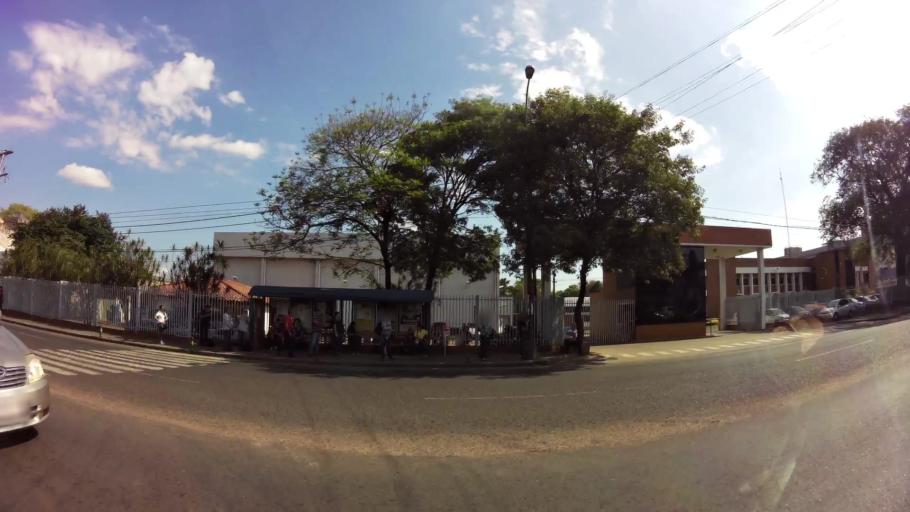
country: PY
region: Central
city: Fernando de la Mora
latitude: -25.3347
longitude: -57.5347
